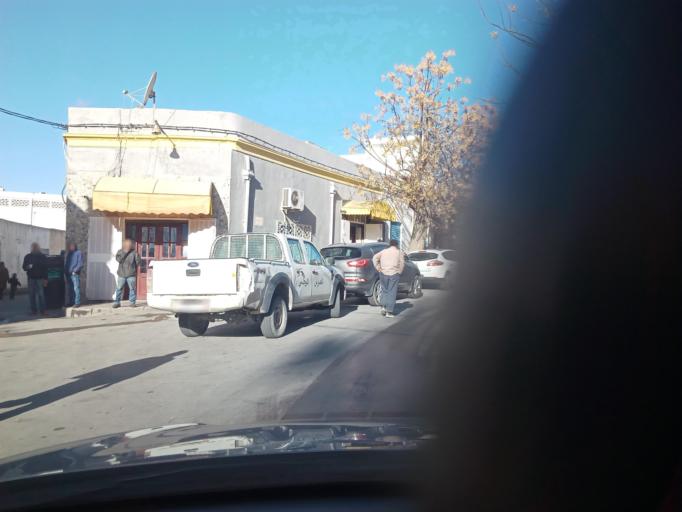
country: TN
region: Kef
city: El Kef
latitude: 36.1799
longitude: 8.7097
